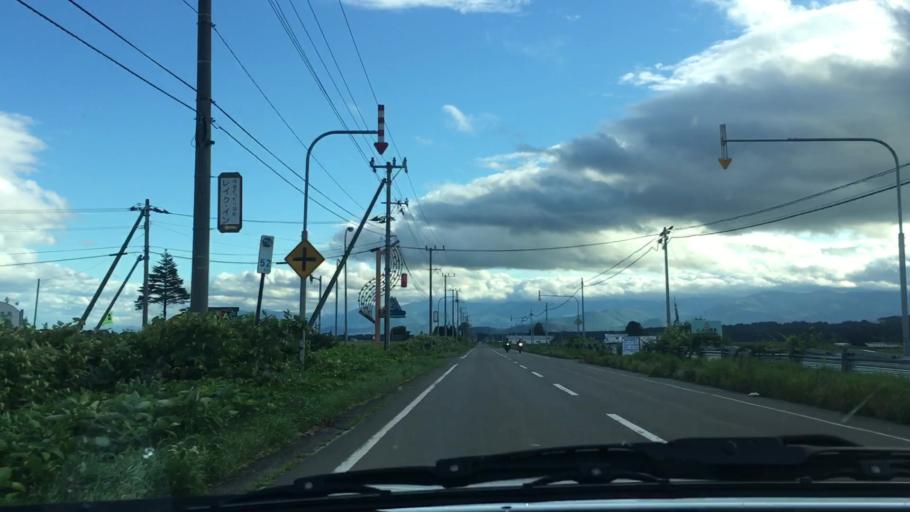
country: JP
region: Hokkaido
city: Otofuke
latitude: 43.1588
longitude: 142.9035
